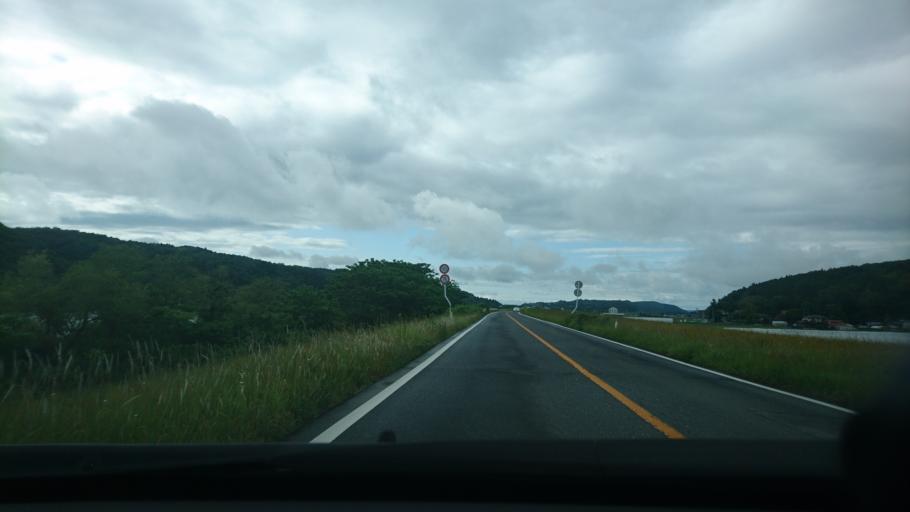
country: JP
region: Miyagi
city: Wakuya
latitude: 38.6309
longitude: 141.2914
